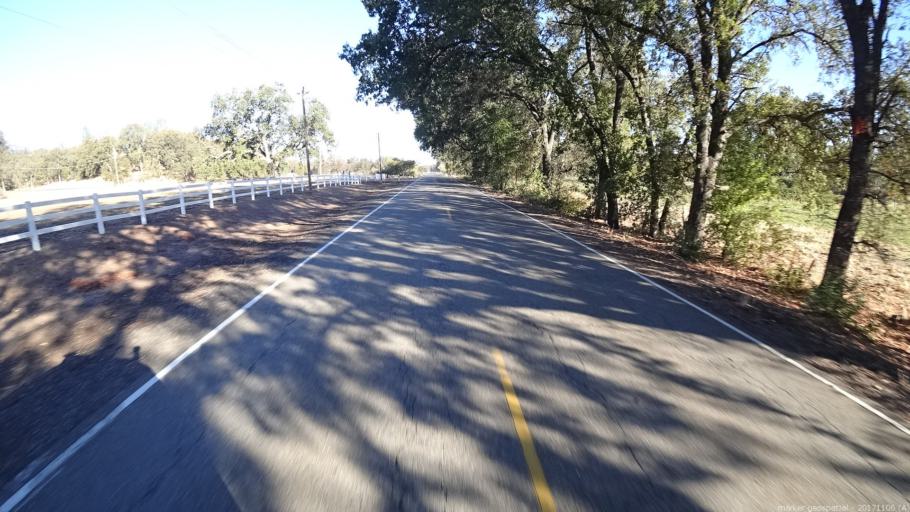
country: US
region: California
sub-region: Shasta County
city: Palo Cedro
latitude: 40.5176
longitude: -122.2385
